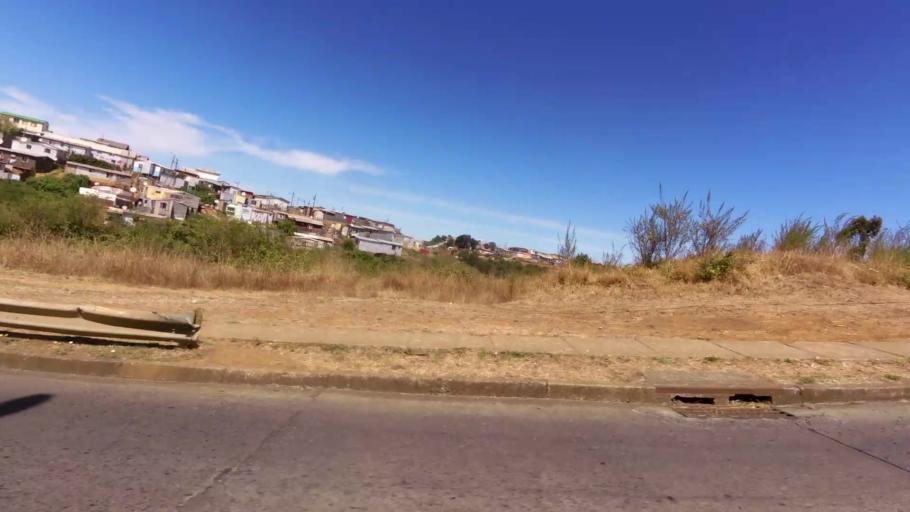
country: CL
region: Biobio
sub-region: Provincia de Concepcion
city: Talcahuano
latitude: -36.7175
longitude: -73.1425
